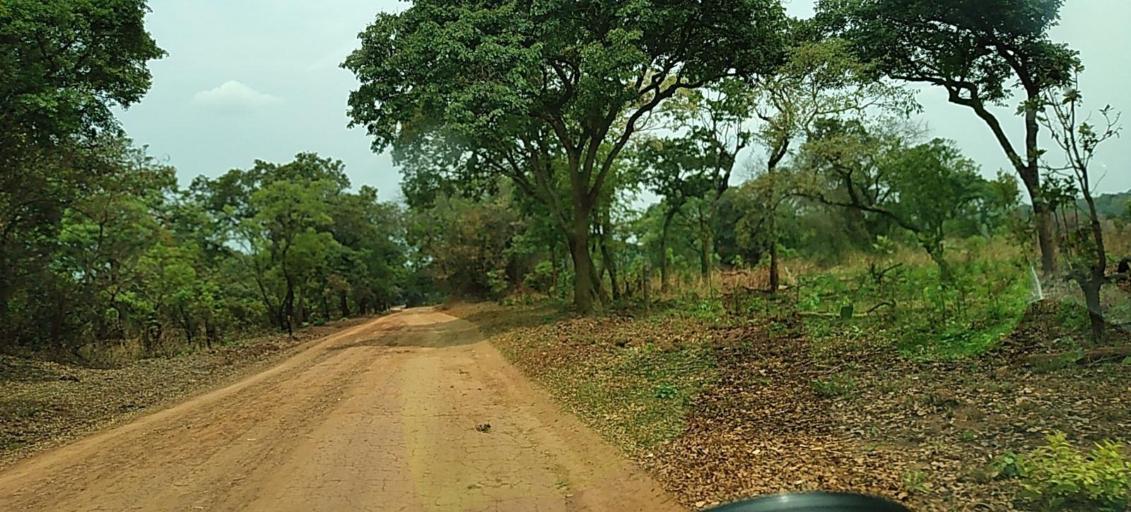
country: ZM
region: North-Western
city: Solwezi
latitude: -12.8181
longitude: 26.5361
